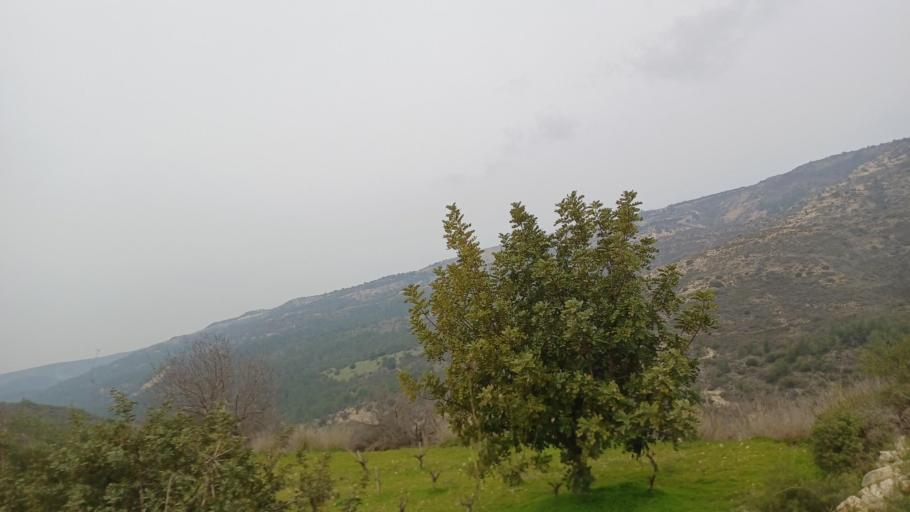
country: CY
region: Limassol
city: Pachna
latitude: 34.7505
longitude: 32.7344
